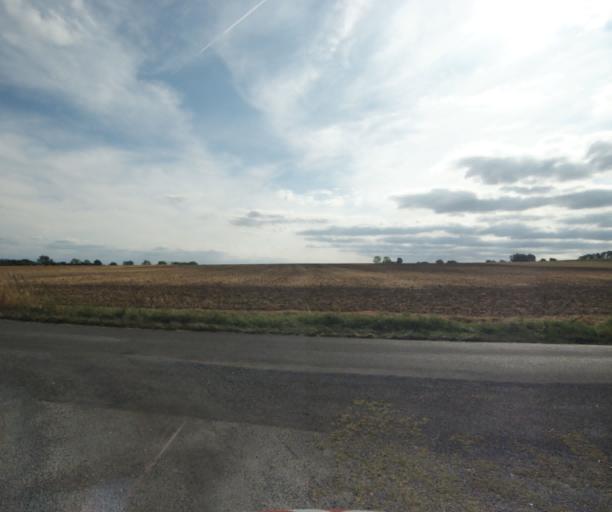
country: FR
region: Midi-Pyrenees
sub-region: Departement du Tarn
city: Puylaurens
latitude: 43.5293
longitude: 1.9977
